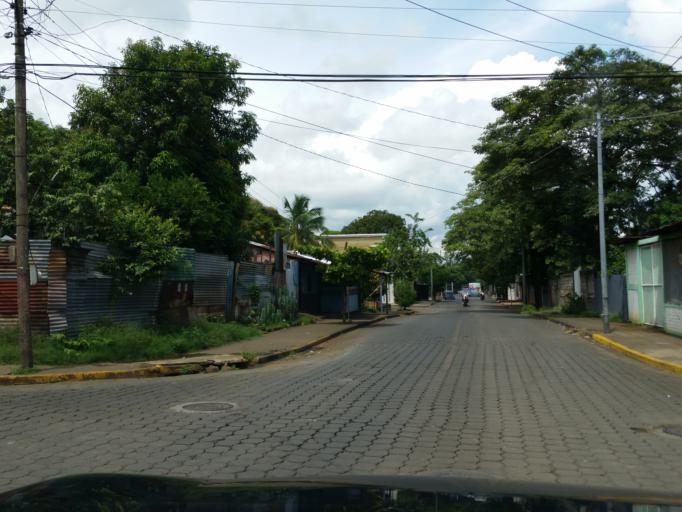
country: NI
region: Managua
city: Managua
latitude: 12.1346
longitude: -86.2511
